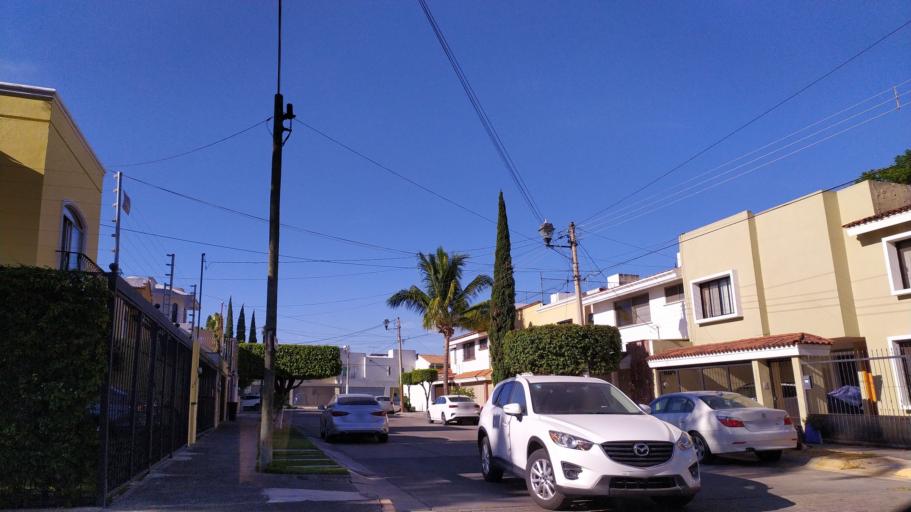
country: MX
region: Jalisco
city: Guadalajara
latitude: 20.6585
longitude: -103.4268
